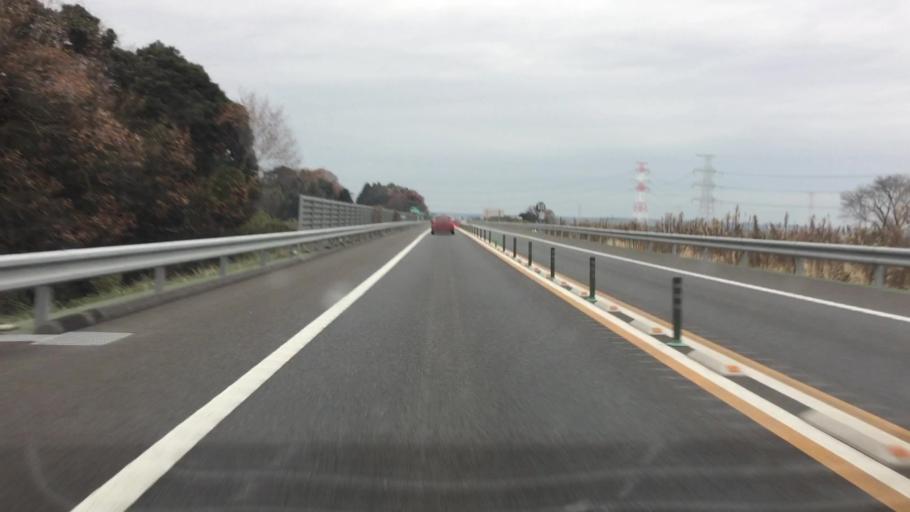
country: JP
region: Ibaraki
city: Edosaki
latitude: 35.8791
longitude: 140.3857
